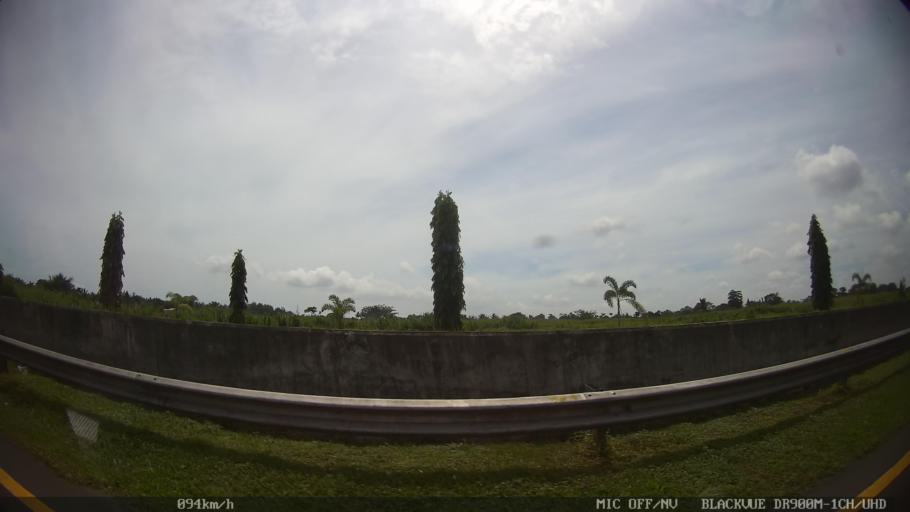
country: ID
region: North Sumatra
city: Labuhan Deli
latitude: 3.7126
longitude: 98.6822
